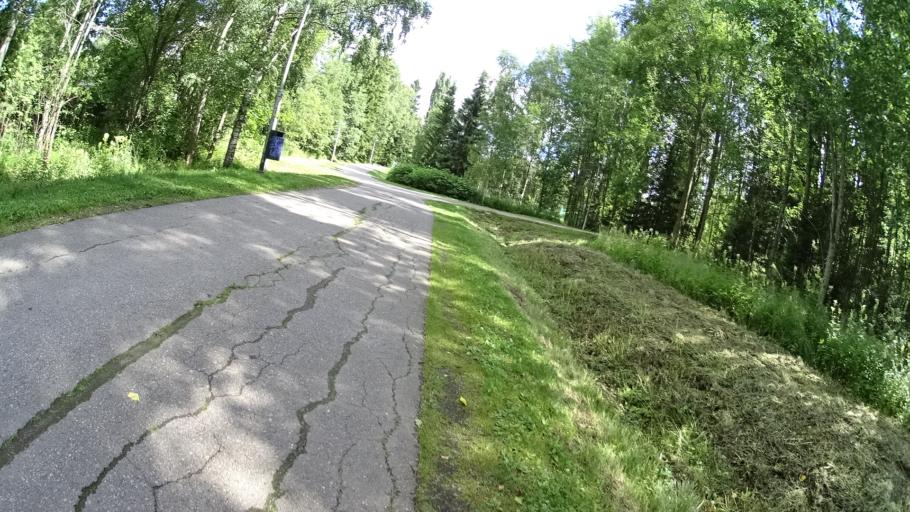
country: FI
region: Uusimaa
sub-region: Helsinki
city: Teekkarikylae
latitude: 60.2741
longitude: 24.8482
